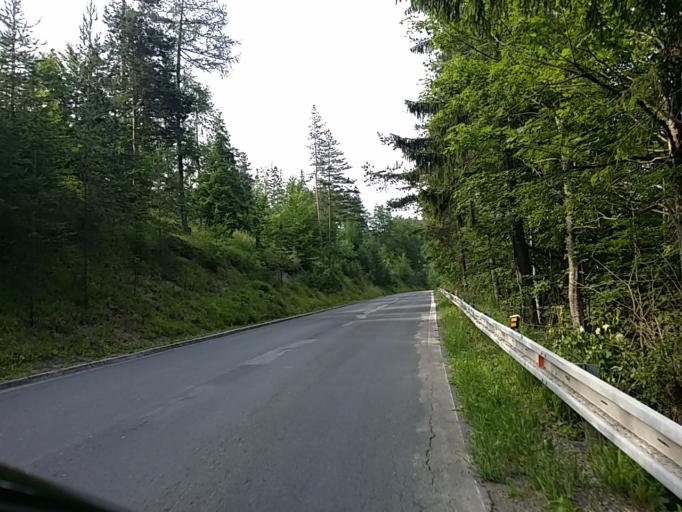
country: SK
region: Kosicky
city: Dobsina
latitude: 48.9040
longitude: 20.2506
